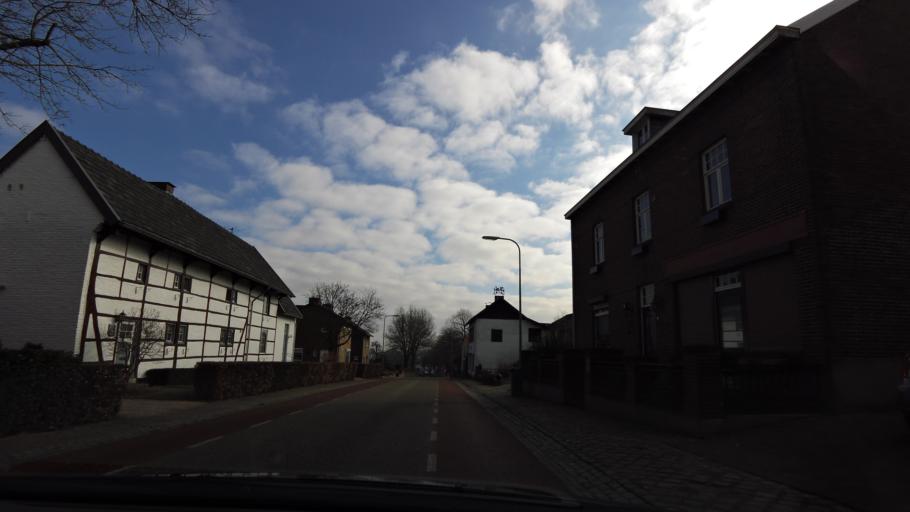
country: BE
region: Wallonia
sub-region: Province de Liege
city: Plombieres
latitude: 50.7726
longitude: 5.8937
